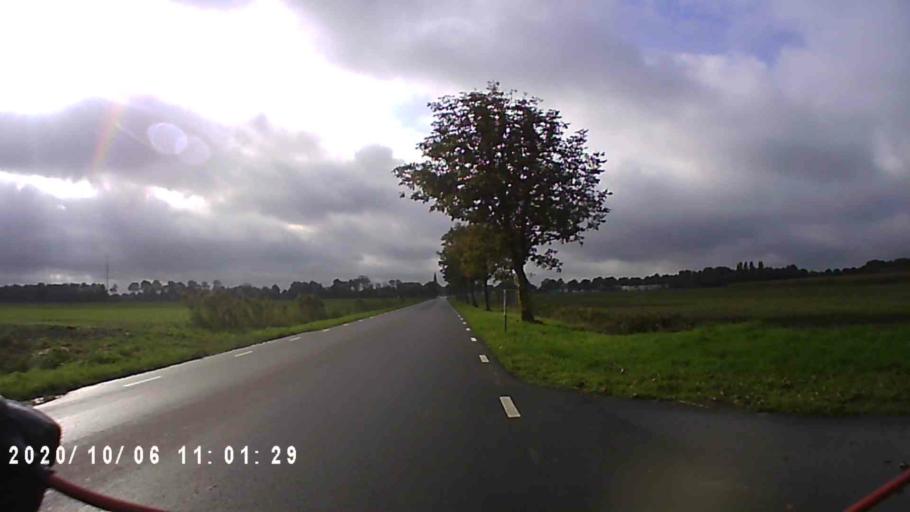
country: NL
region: Groningen
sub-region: Gemeente De Marne
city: Ulrum
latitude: 53.3674
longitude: 6.3734
